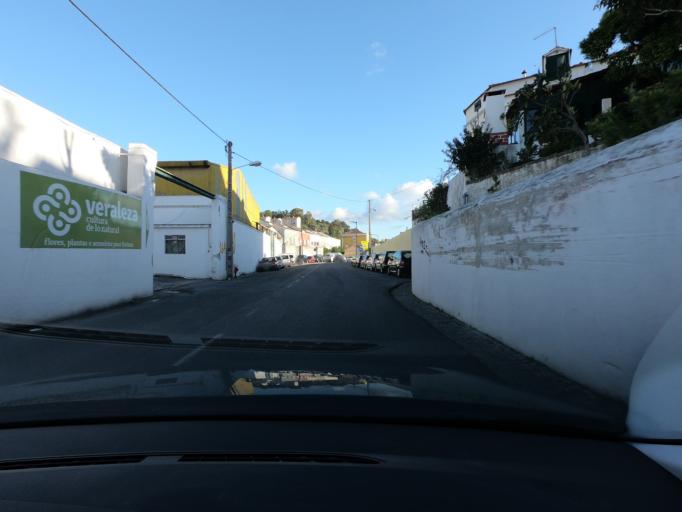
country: PT
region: Lisbon
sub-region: Lisbon
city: Lisbon
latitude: 38.7369
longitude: -9.1171
